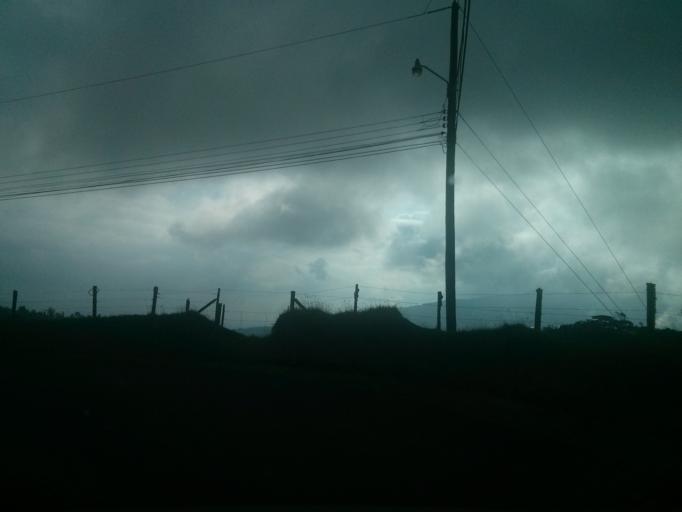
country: CR
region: Heredia
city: Santo Domingo
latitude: 10.1427
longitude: -84.1588
